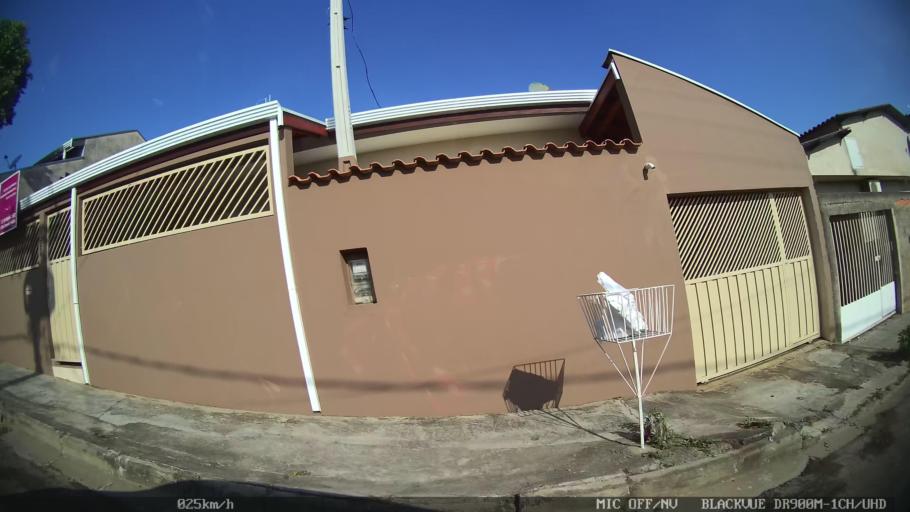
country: BR
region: Sao Paulo
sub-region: Indaiatuba
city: Indaiatuba
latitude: -22.9856
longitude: -47.1515
